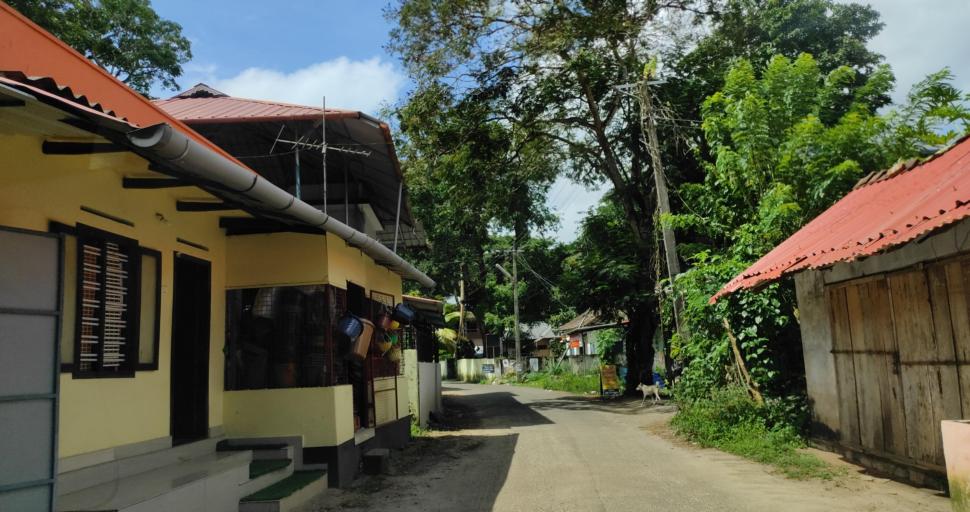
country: IN
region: Kerala
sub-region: Alappuzha
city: Shertallai
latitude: 9.6755
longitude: 76.3929
